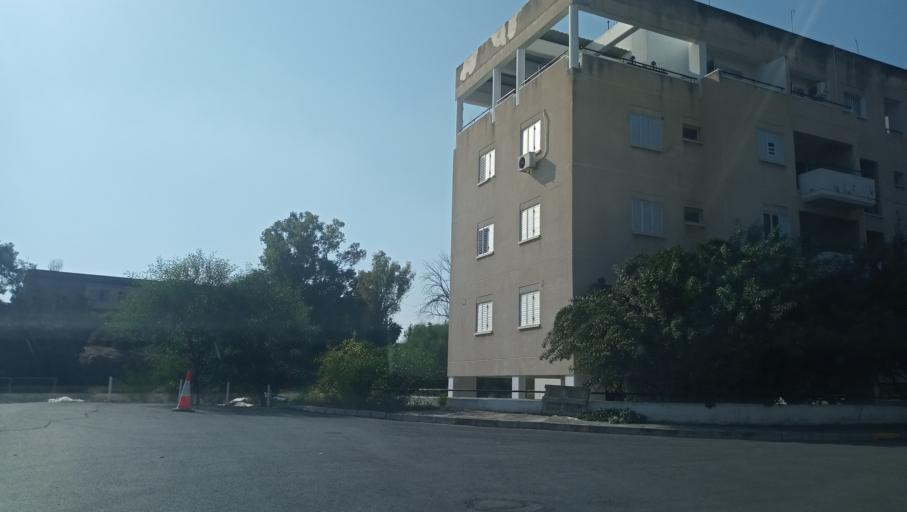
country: CY
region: Lefkosia
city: Nicosia
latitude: 35.1511
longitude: 33.3775
